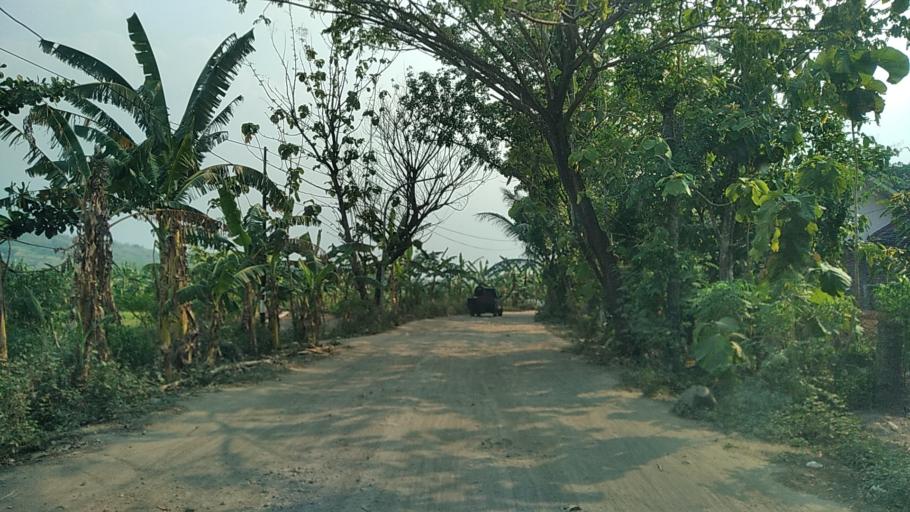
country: ID
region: Central Java
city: Mranggen
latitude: -7.0711
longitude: 110.4716
